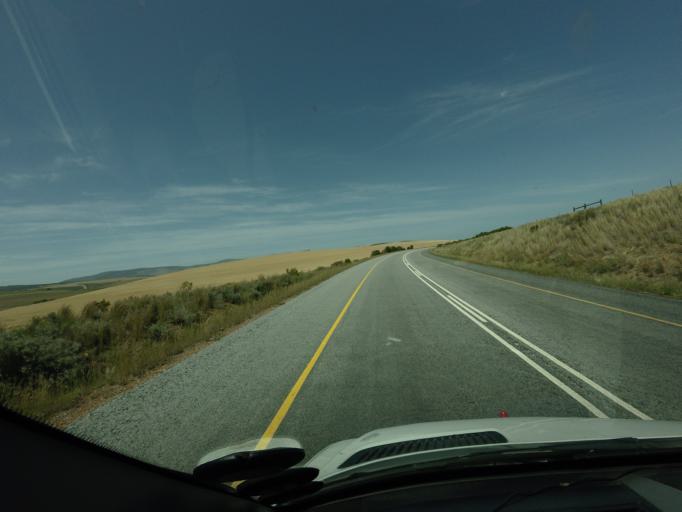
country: ZA
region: Western Cape
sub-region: Overberg District Municipality
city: Hermanus
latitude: -34.3171
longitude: 19.1488
